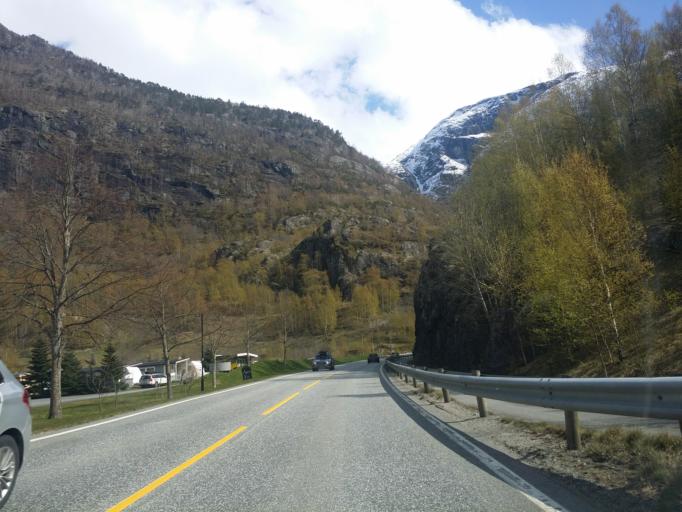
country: NO
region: Hordaland
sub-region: Eidfjord
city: Eidfjord
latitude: 60.4231
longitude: 7.1377
